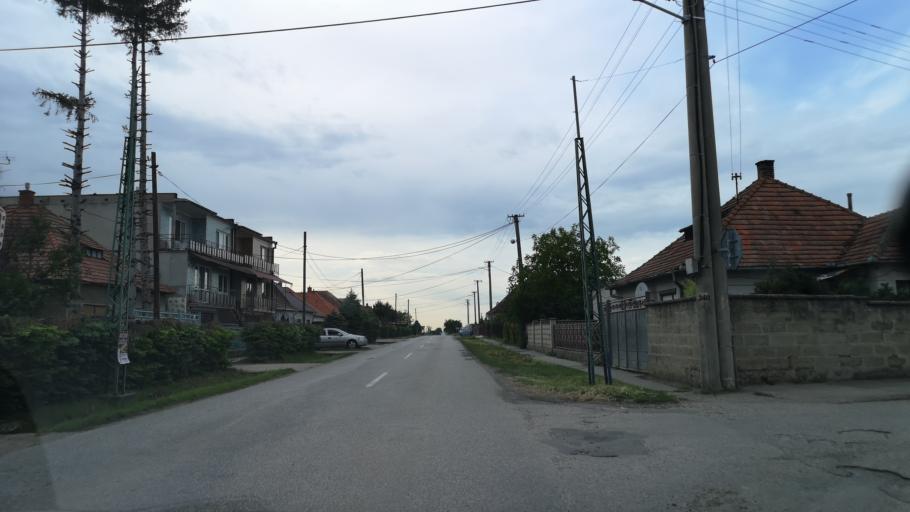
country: SK
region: Nitriansky
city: Sellye
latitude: 48.2454
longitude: 17.9080
